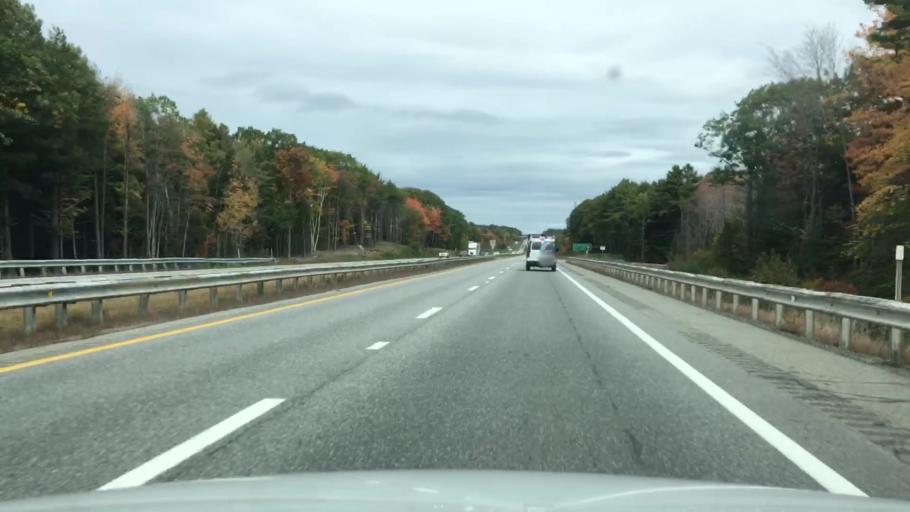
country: US
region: Maine
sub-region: Kennebec County
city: Farmingdale
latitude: 44.2476
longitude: -69.8074
